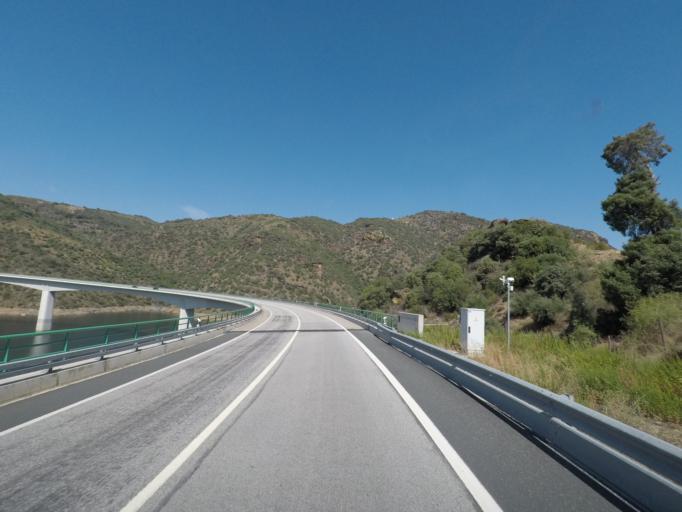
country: PT
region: Braganca
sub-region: Alfandega da Fe
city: Alfandega da Fe
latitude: 41.2859
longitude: -6.8714
